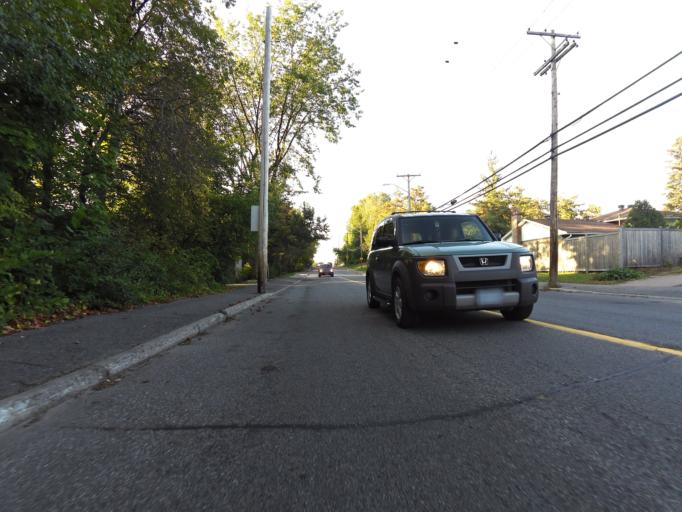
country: CA
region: Ontario
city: Ottawa
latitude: 45.3627
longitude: -75.6761
